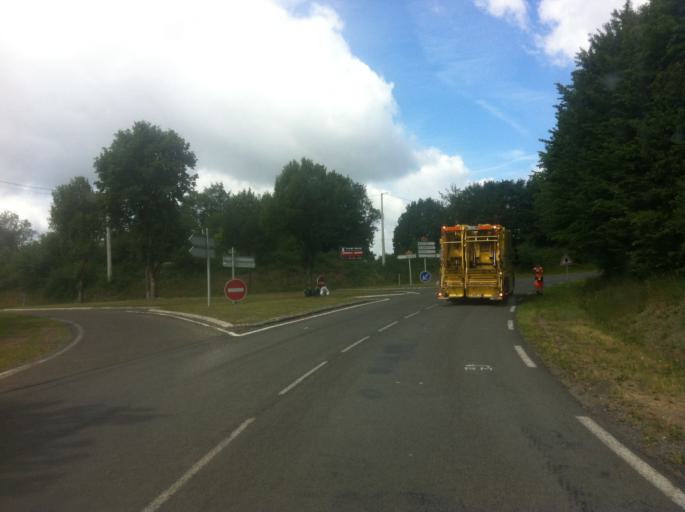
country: FR
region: Nord-Pas-de-Calais
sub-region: Departement du Nord
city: Trelon
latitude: 50.1252
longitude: 4.1482
